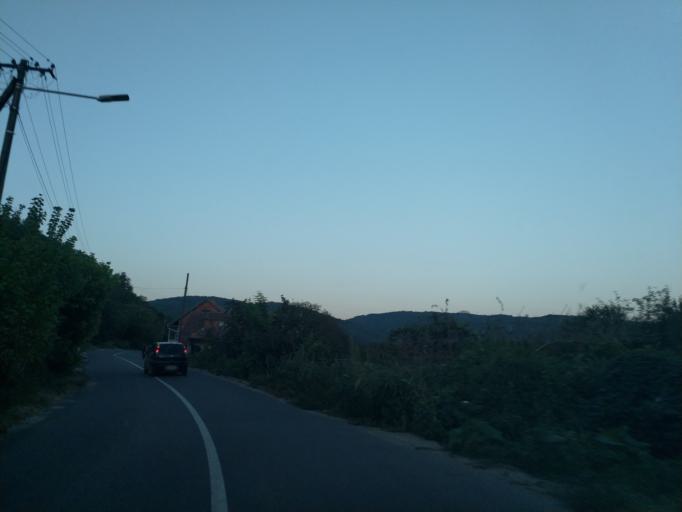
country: RS
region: Central Serbia
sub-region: Rasinski Okrug
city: Krusevac
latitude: 43.6238
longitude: 21.3613
